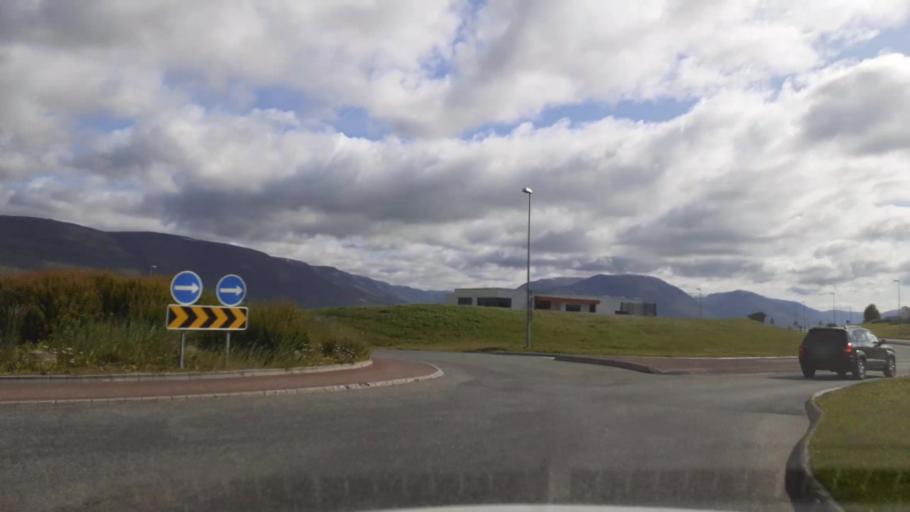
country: IS
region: Northeast
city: Akureyri
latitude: 65.6649
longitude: -18.0902
